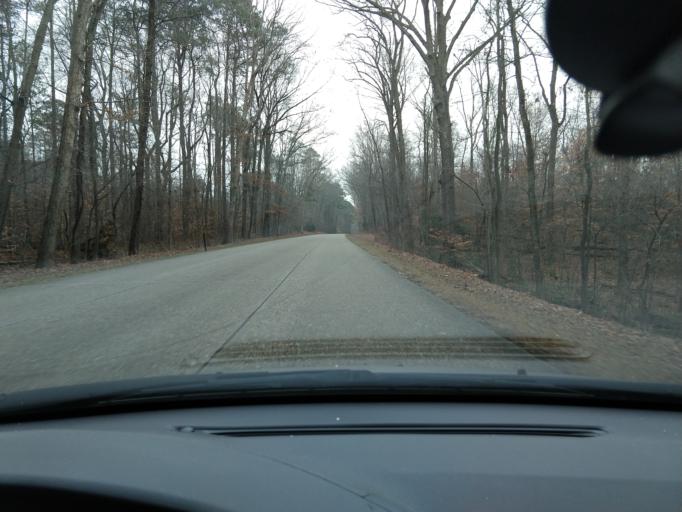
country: US
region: Virginia
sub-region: City of Williamsburg
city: Williamsburg
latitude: 37.2781
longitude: -76.6187
